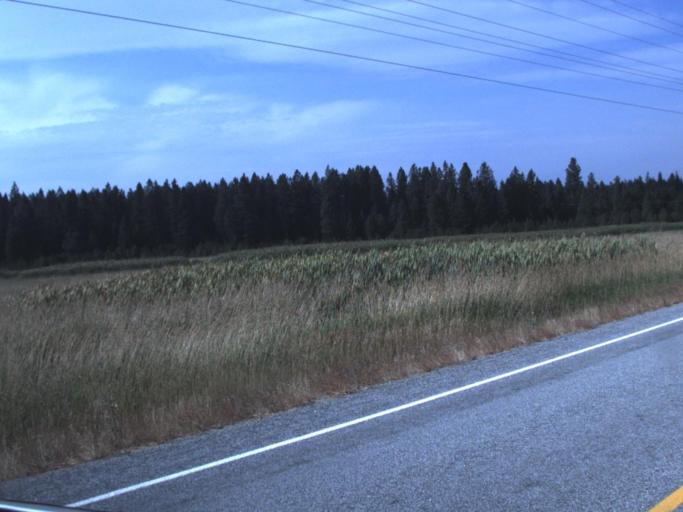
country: US
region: Washington
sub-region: Pend Oreille County
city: Newport
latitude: 48.2892
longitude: -117.2845
